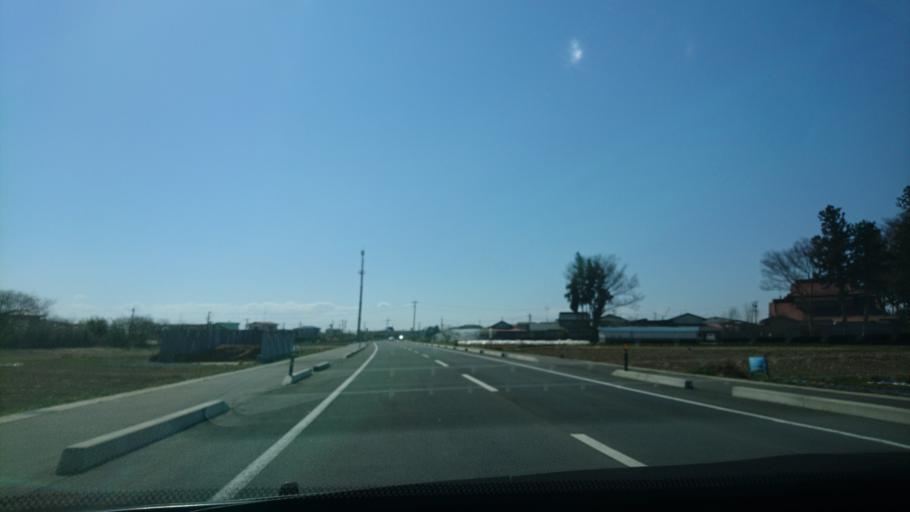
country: JP
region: Iwate
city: Ichinoseki
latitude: 38.7747
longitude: 141.1434
